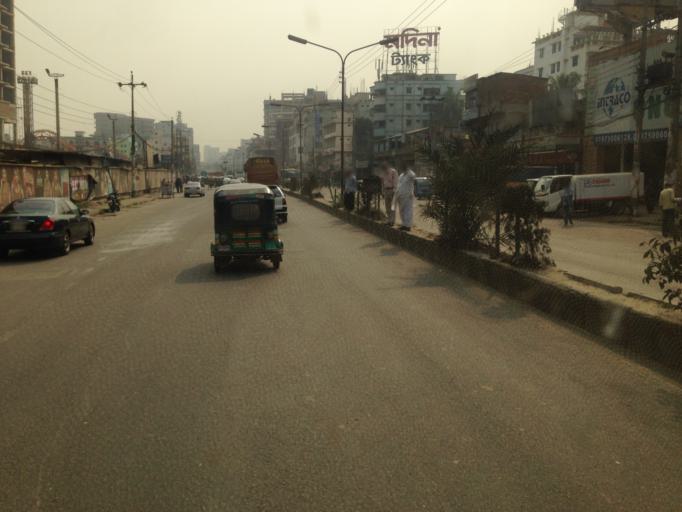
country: BD
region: Dhaka
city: Paltan
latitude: 23.8145
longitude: 90.4212
